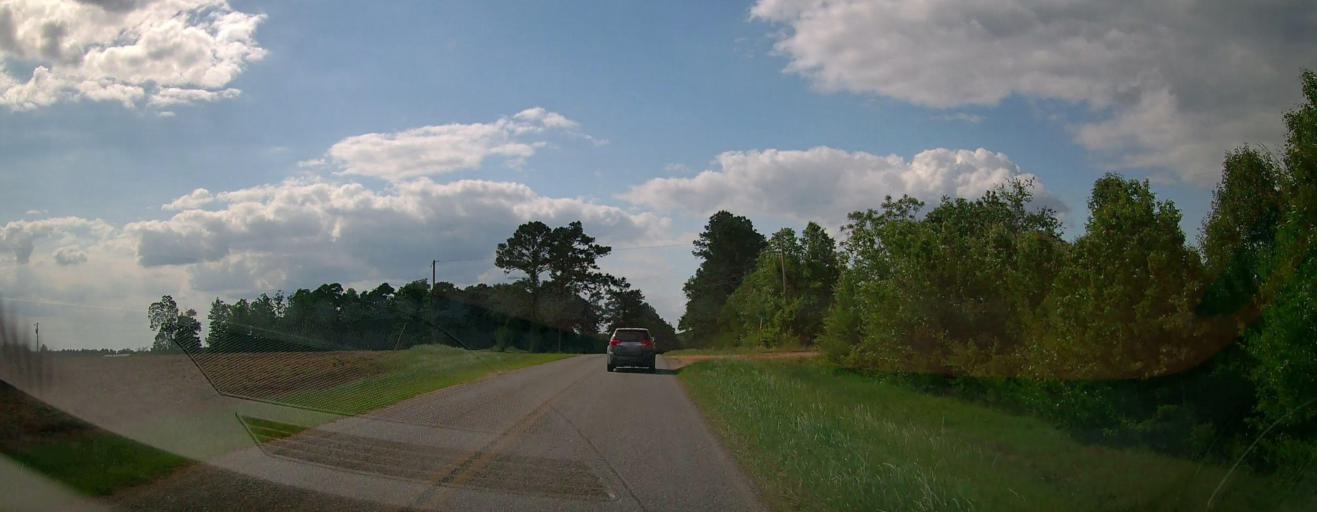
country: US
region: Georgia
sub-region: Laurens County
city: East Dublin
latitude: 32.6962
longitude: -82.9090
